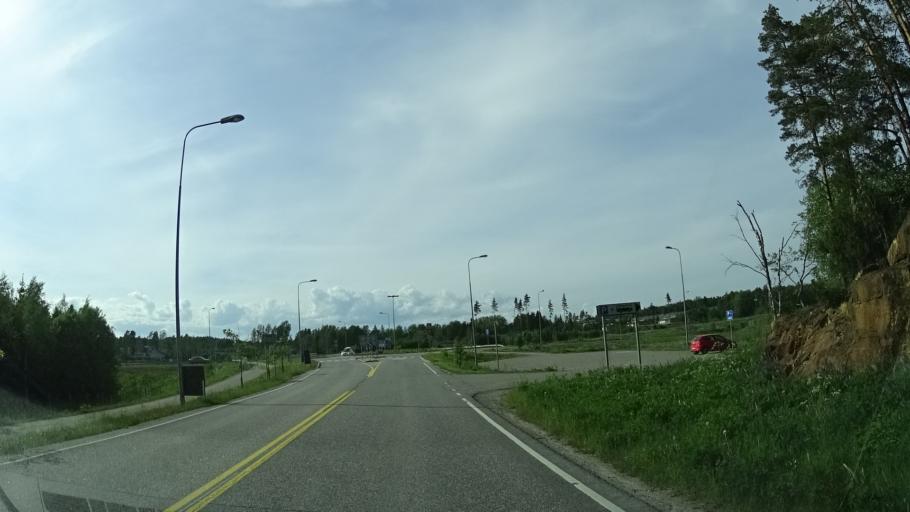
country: FI
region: Uusimaa
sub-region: Helsinki
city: Kirkkonummi
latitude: 60.1180
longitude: 24.4813
